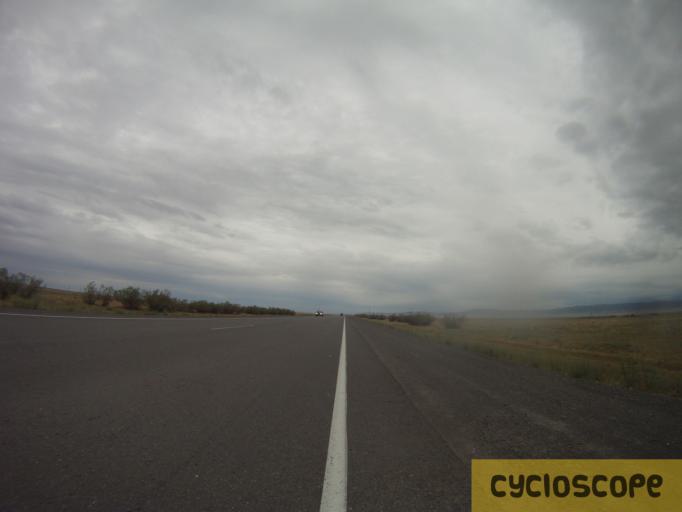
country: KG
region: Chuy
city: Ivanovka
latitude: 43.3943
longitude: 75.1311
